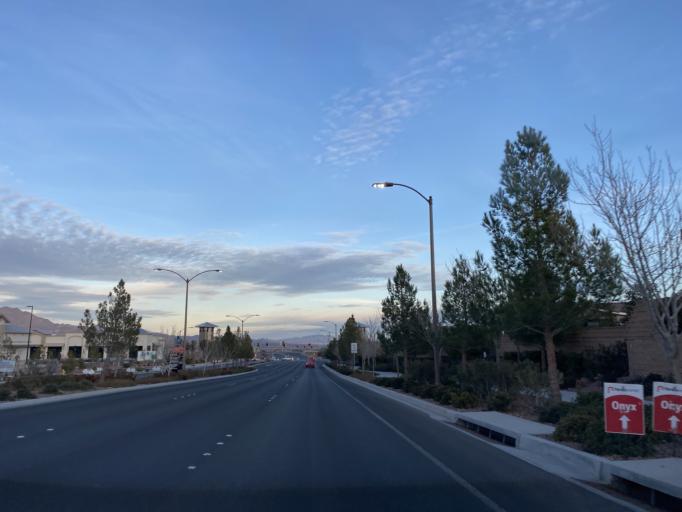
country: US
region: Nevada
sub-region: Clark County
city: Summerlin South
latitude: 36.3140
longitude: -115.3085
